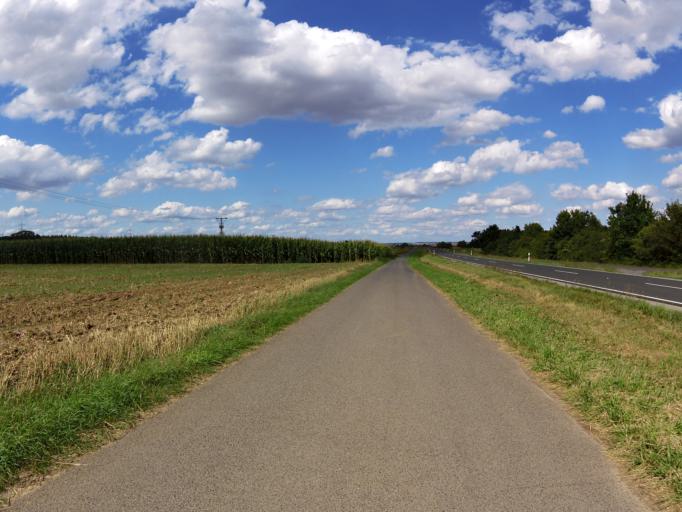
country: DE
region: Bavaria
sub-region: Regierungsbezirk Unterfranken
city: Bergrheinfeld
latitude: 49.9893
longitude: 10.1695
